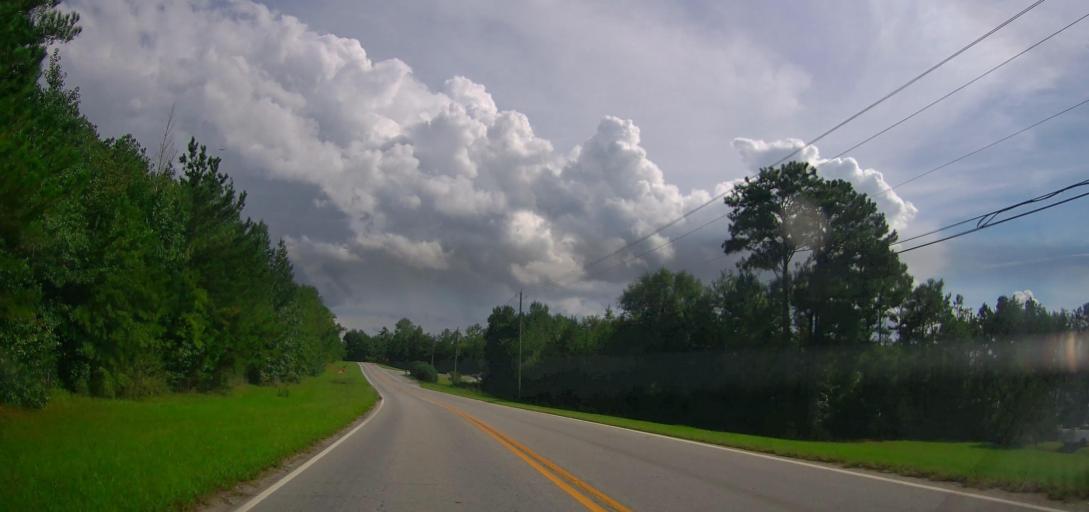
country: US
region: Alabama
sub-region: Russell County
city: Phenix City
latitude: 32.5978
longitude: -84.9489
